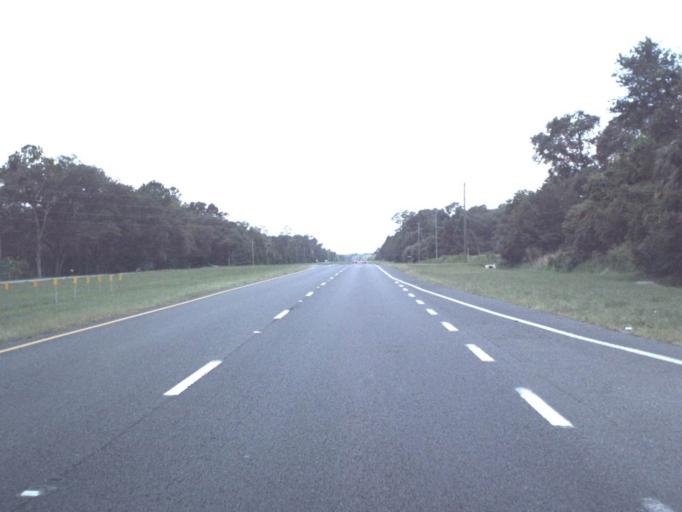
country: US
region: Florida
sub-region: Alachua County
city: Hawthorne
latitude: 29.5983
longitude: -82.1166
